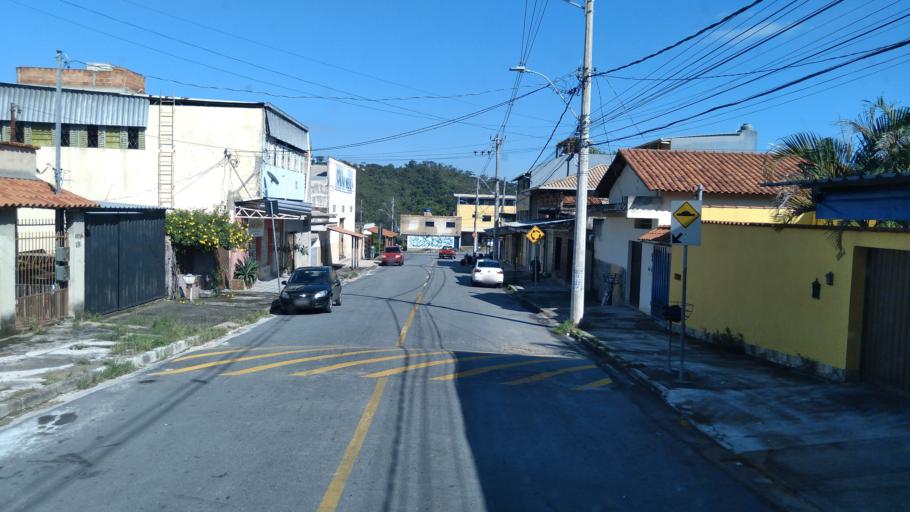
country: BR
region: Minas Gerais
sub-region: Santa Luzia
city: Santa Luzia
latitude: -19.8275
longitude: -43.9011
